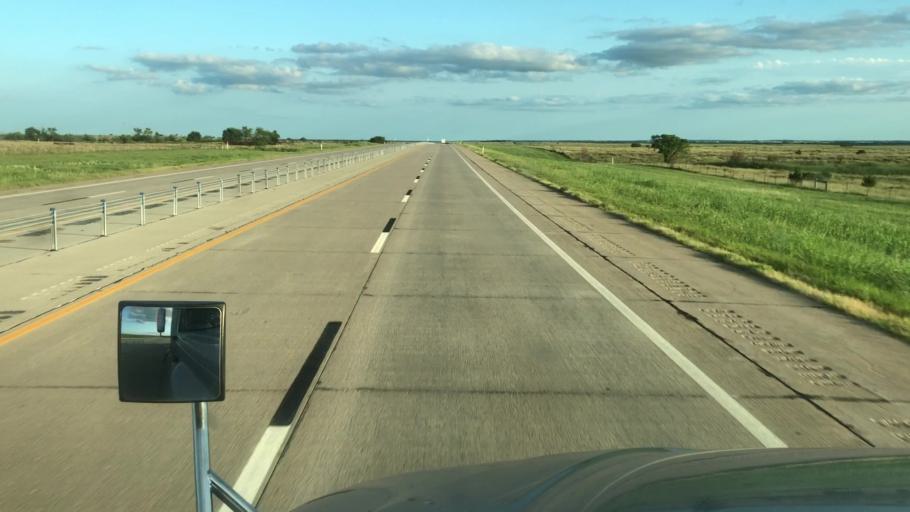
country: US
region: Oklahoma
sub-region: Pawnee County
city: Pawnee
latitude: 36.3648
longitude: -97.0345
